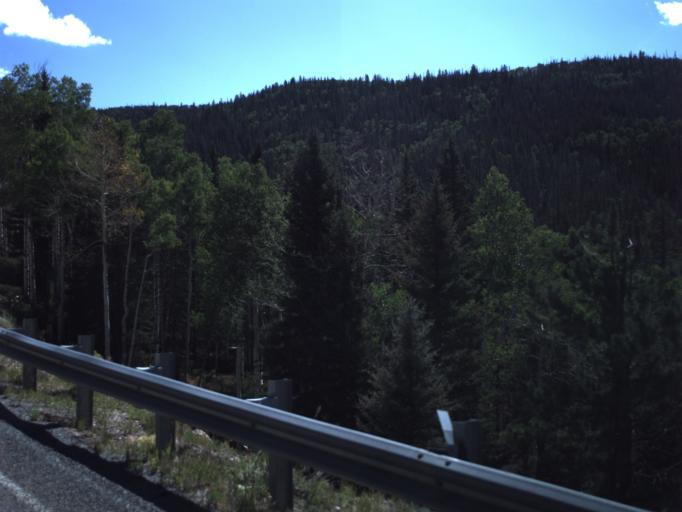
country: US
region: Utah
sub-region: Piute County
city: Junction
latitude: 38.3077
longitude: -112.4072
